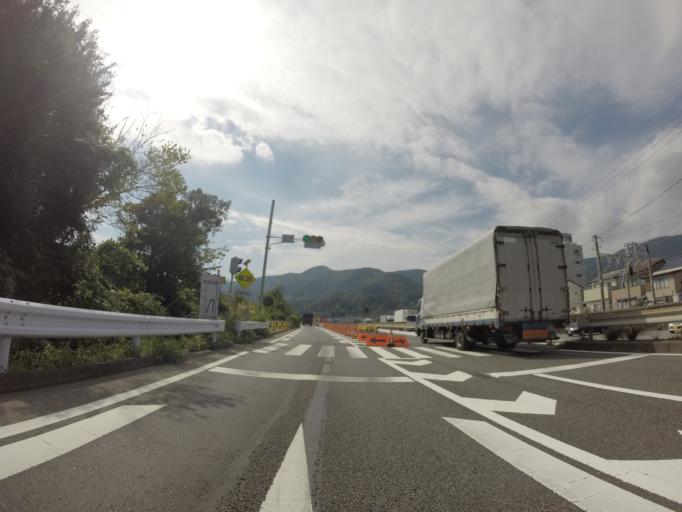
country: JP
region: Shizuoka
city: Fujinomiya
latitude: 35.1045
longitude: 138.5629
